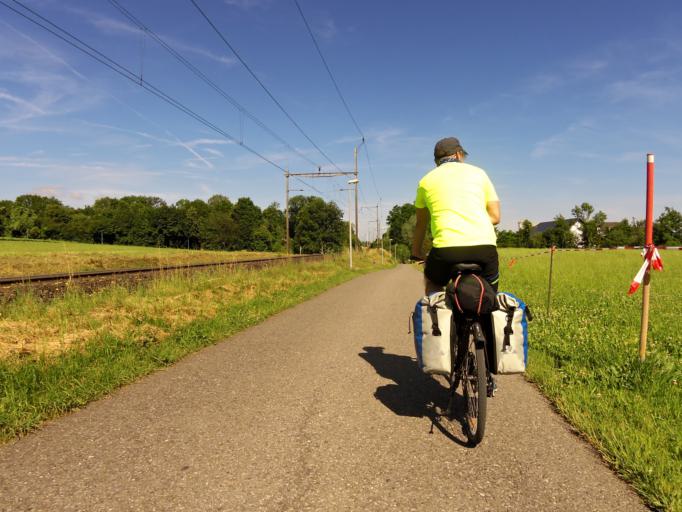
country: CH
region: Thurgau
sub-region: Kreuzlingen District
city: Bottighofen
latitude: 47.6413
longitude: 9.2122
